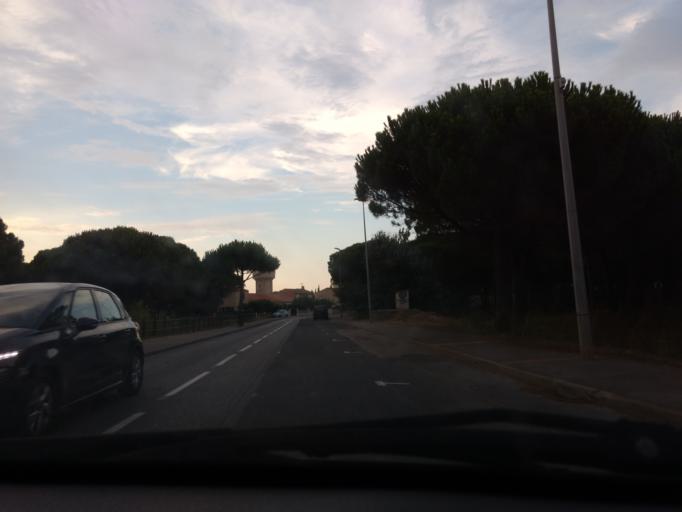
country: FR
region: Languedoc-Roussillon
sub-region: Departement des Pyrenees-Orientales
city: Le Barcares
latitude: 42.7841
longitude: 3.0337
